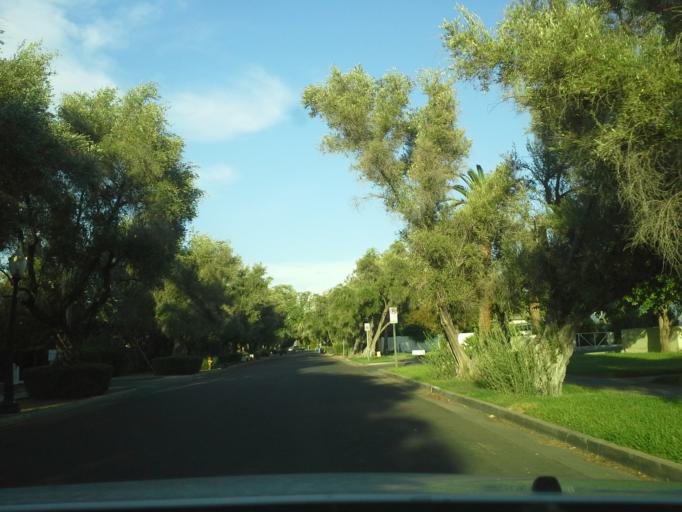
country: US
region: Arizona
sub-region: Maricopa County
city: Phoenix
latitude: 33.4711
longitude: -112.0722
